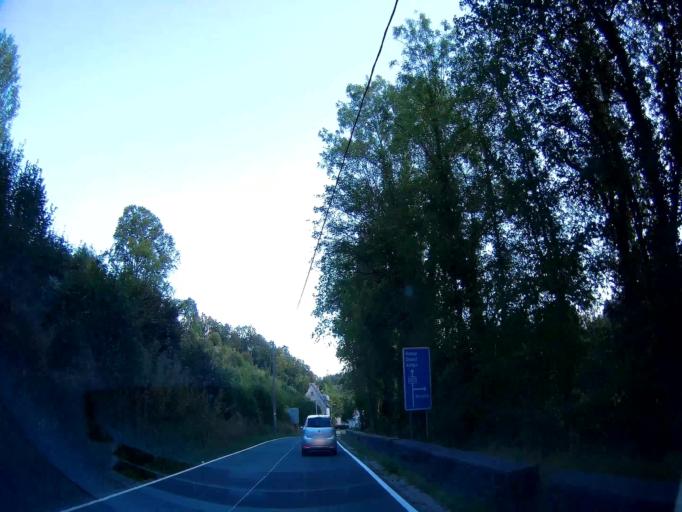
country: BE
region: Wallonia
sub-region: Province de Namur
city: Onhaye
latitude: 50.3064
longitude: 4.7680
